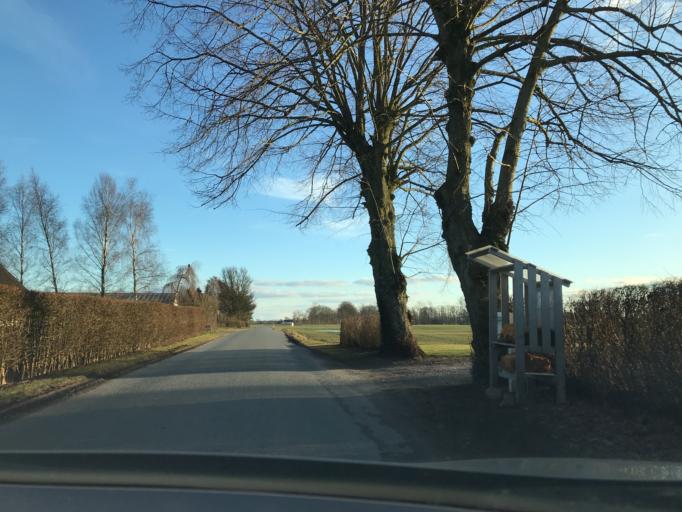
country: DK
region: South Denmark
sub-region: Middelfart Kommune
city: Brenderup
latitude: 55.5141
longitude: 10.0240
